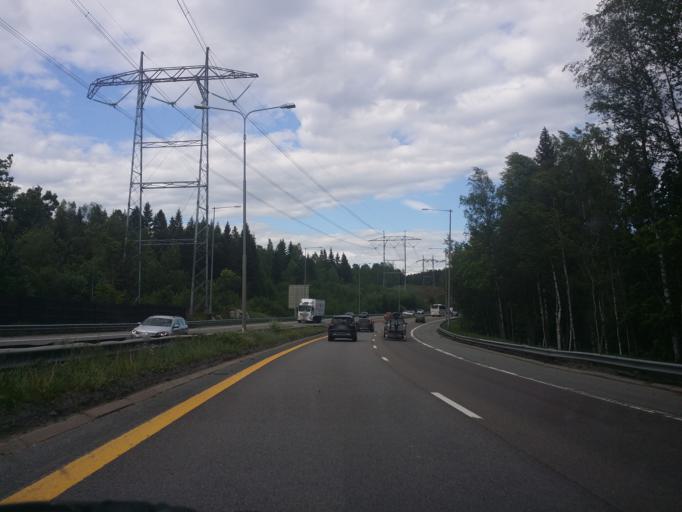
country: NO
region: Akershus
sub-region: Lorenskog
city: Kjenn
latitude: 59.9255
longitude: 10.8514
